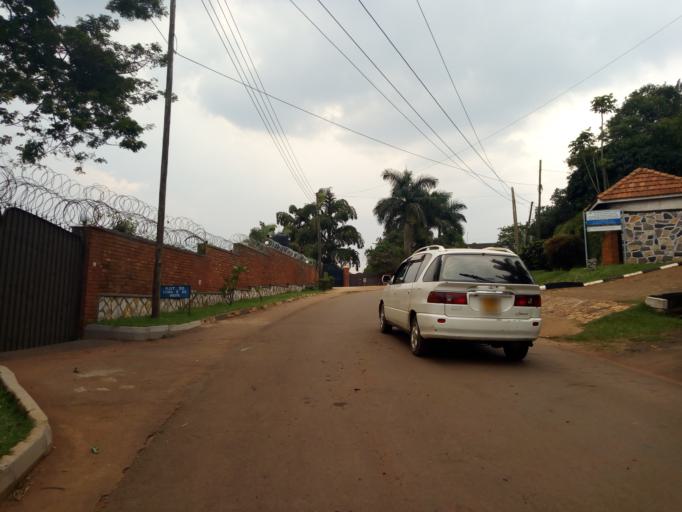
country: UG
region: Central Region
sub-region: Wakiso District
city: Kireka
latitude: 0.3272
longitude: 32.6260
